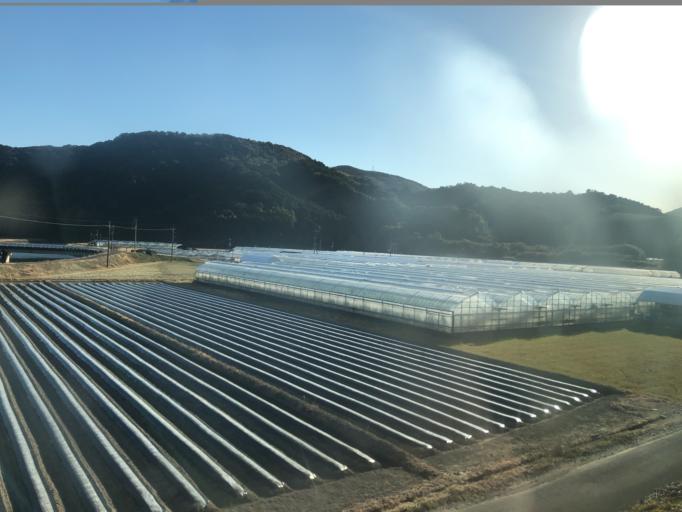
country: JP
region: Kochi
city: Nakamura
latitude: 33.0146
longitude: 132.9949
